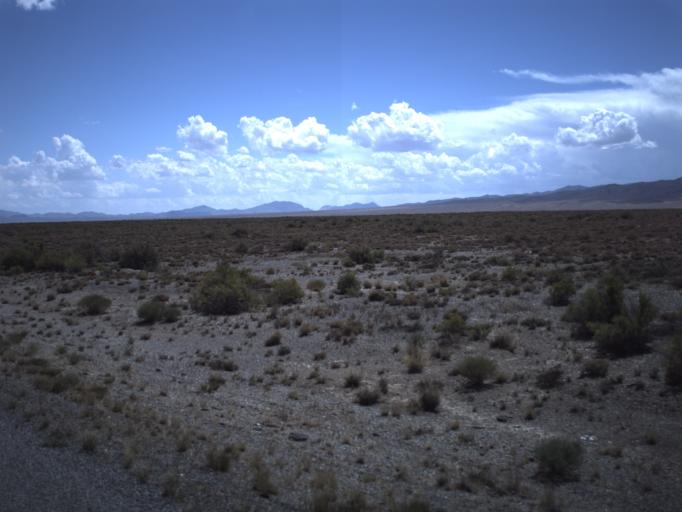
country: US
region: Nevada
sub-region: White Pine County
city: McGill
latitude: 39.0506
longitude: -113.9630
